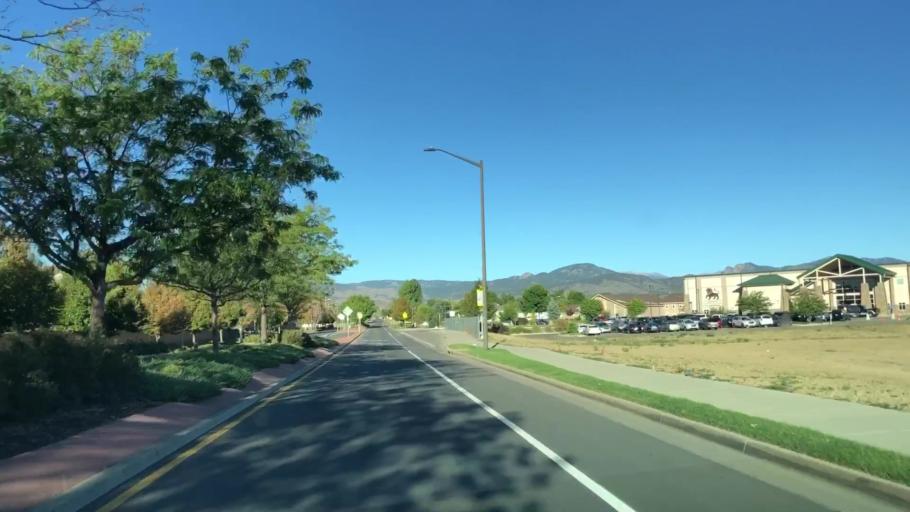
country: US
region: Colorado
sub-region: Larimer County
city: Loveland
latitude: 40.3784
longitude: -105.1282
